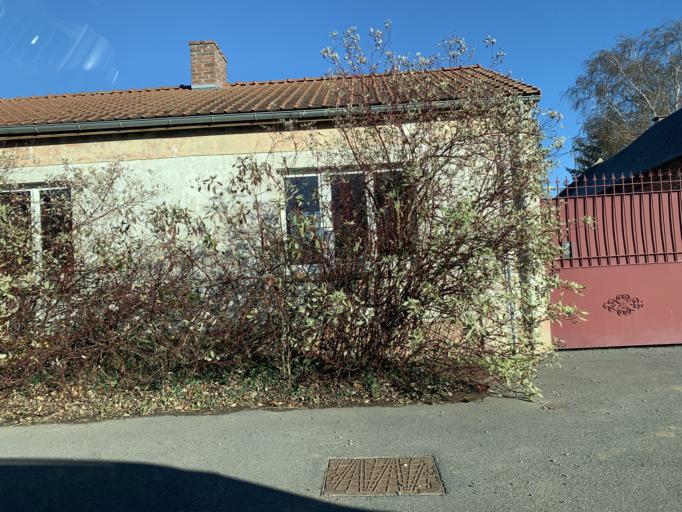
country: FR
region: Nord-Pas-de-Calais
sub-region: Departement du Nord
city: Rieux-en-Cambresis
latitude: 50.1542
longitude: 3.3247
